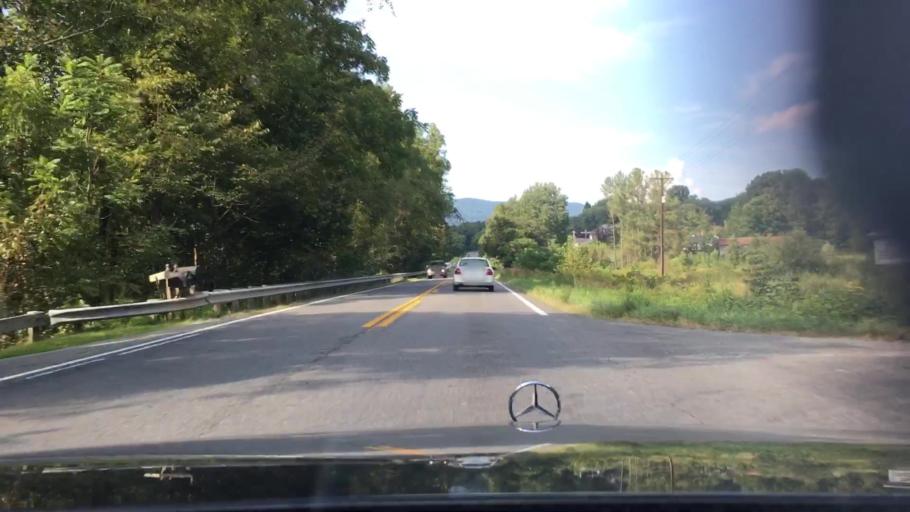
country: US
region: Virginia
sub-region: Nelson County
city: Nellysford
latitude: 37.9827
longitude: -78.8391
